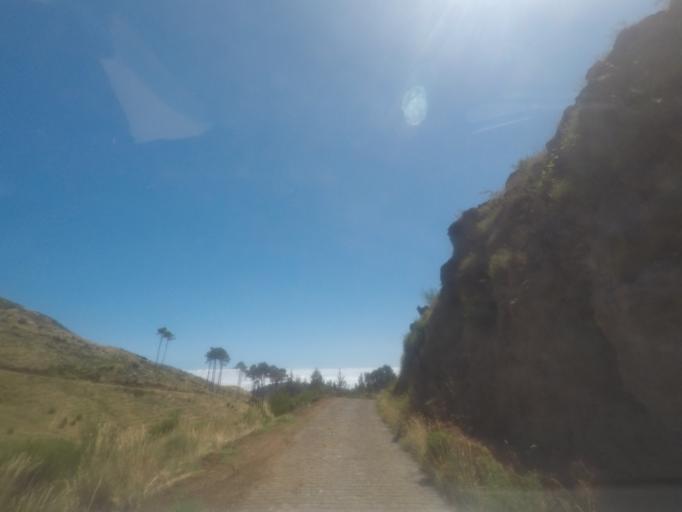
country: PT
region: Madeira
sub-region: Funchal
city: Nossa Senhora do Monte
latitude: 32.7039
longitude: -16.9026
